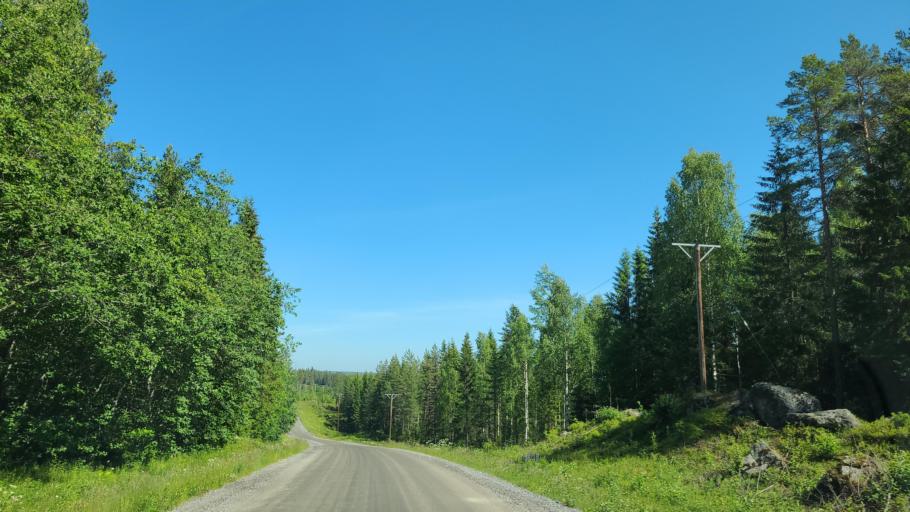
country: SE
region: Vaesterbotten
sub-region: Bjurholms Kommun
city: Bjurholm
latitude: 63.6389
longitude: 19.1969
